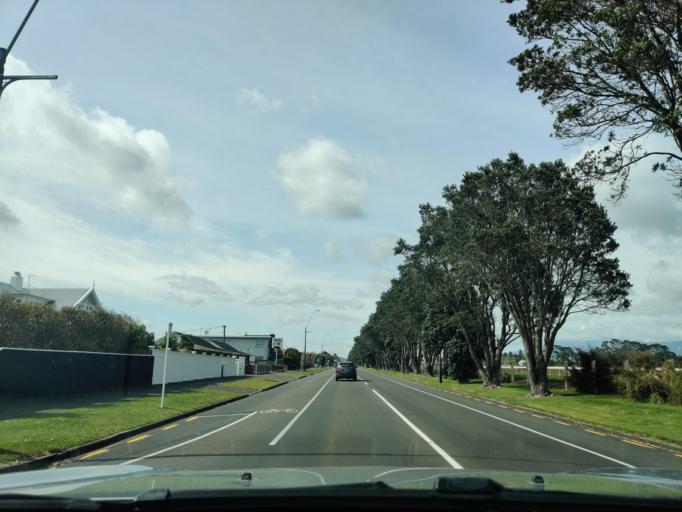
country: NZ
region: Taranaki
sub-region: New Plymouth District
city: New Plymouth
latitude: -39.0638
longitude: 174.0871
